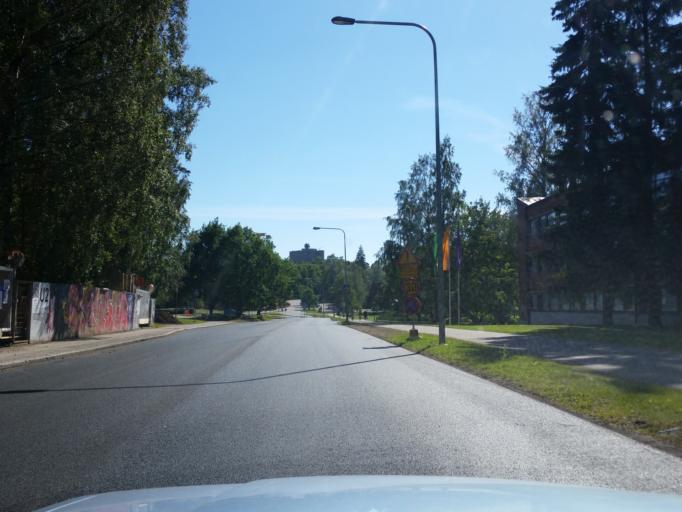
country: FI
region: Uusimaa
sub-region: Helsinki
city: Otaniemi
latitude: 60.1874
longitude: 24.8280
